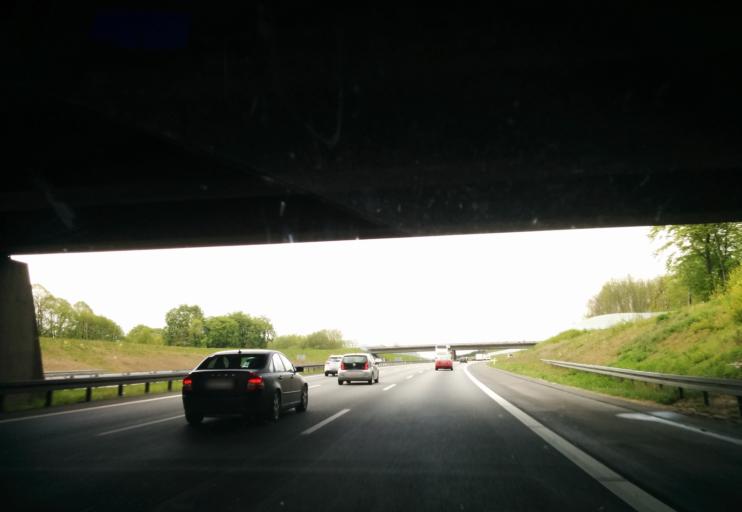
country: DK
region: South Denmark
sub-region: Vejle Kommune
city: Vejle
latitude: 55.6834
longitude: 9.5639
